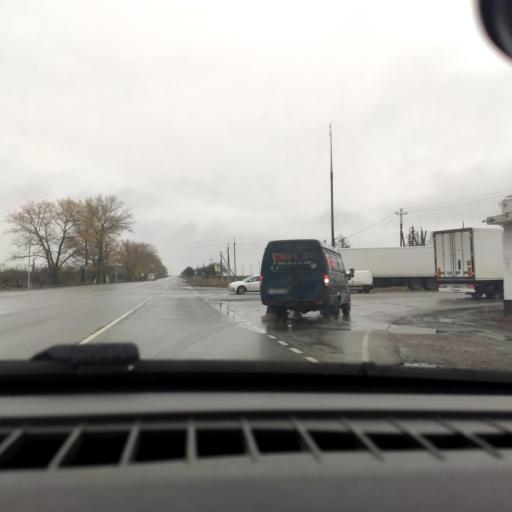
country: RU
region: Belgorod
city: Ilovka
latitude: 50.7092
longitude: 38.6537
